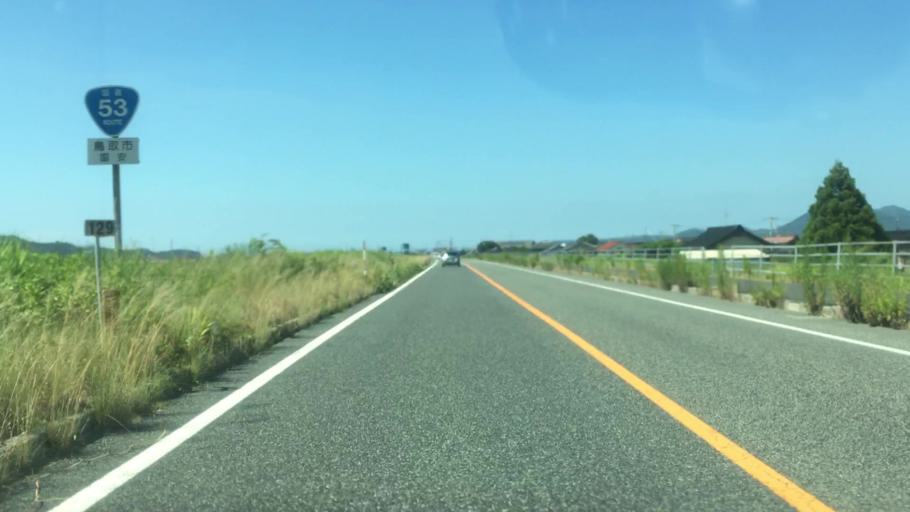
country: JP
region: Tottori
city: Tottori
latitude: 35.4577
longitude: 134.2152
